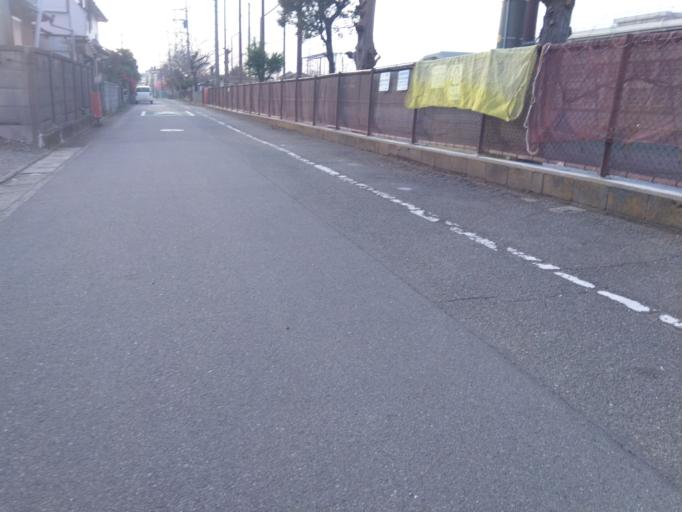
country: JP
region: Kanagawa
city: Hiratsuka
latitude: 35.3531
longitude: 139.3586
